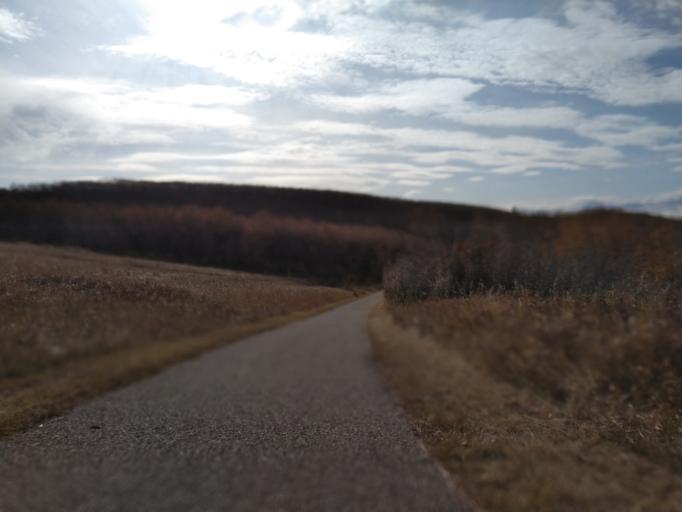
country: CA
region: Alberta
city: Calgary
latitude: 51.1046
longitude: -114.1162
